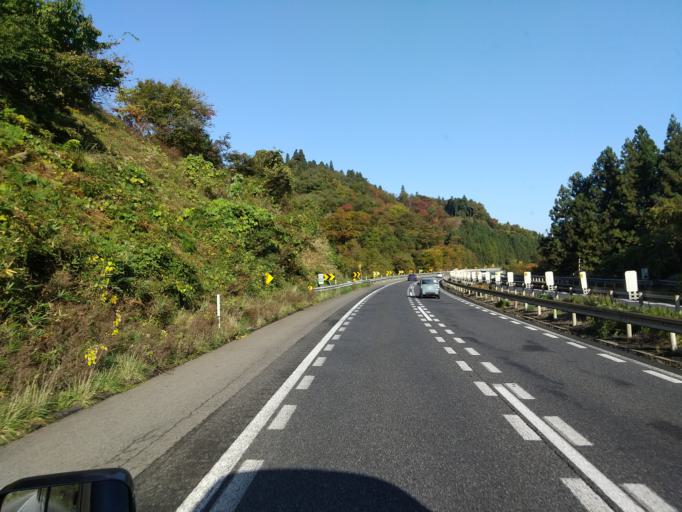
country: JP
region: Iwate
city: Ichinoseki
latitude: 39.0040
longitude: 141.0875
